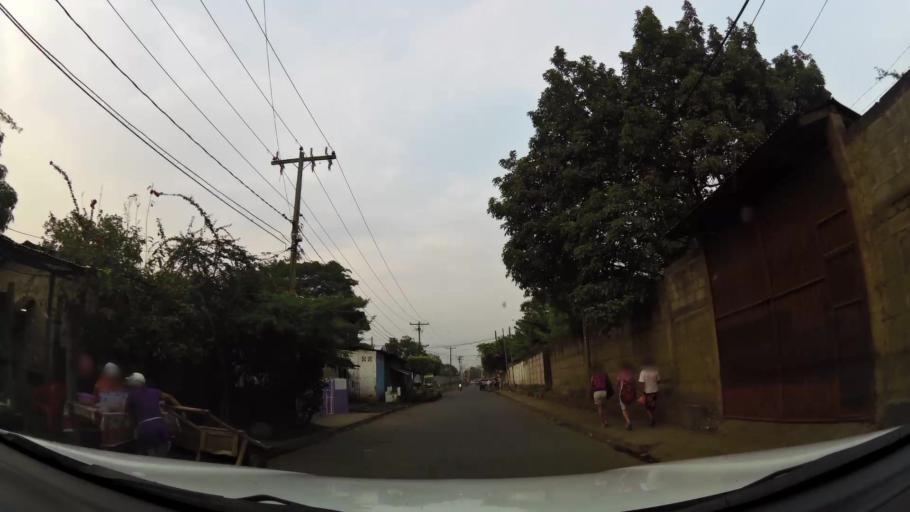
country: NI
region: Masaya
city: Masaya
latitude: 11.9805
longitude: -86.0882
